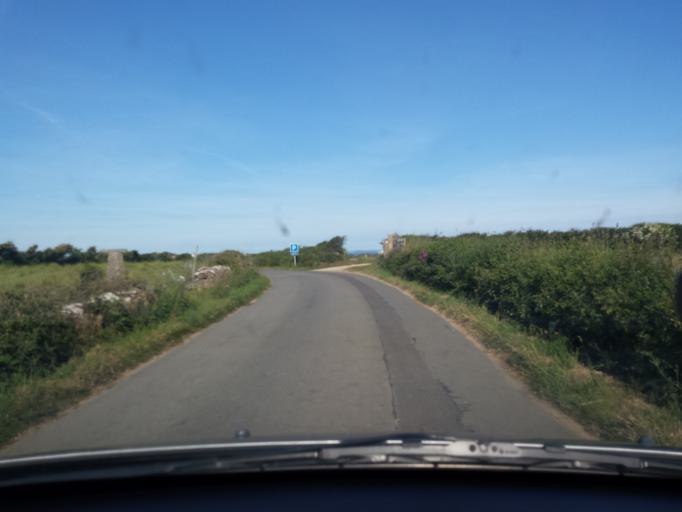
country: FR
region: Lower Normandy
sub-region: Departement de la Manche
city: Beaumont-Hague
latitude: 49.6773
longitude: -1.9360
